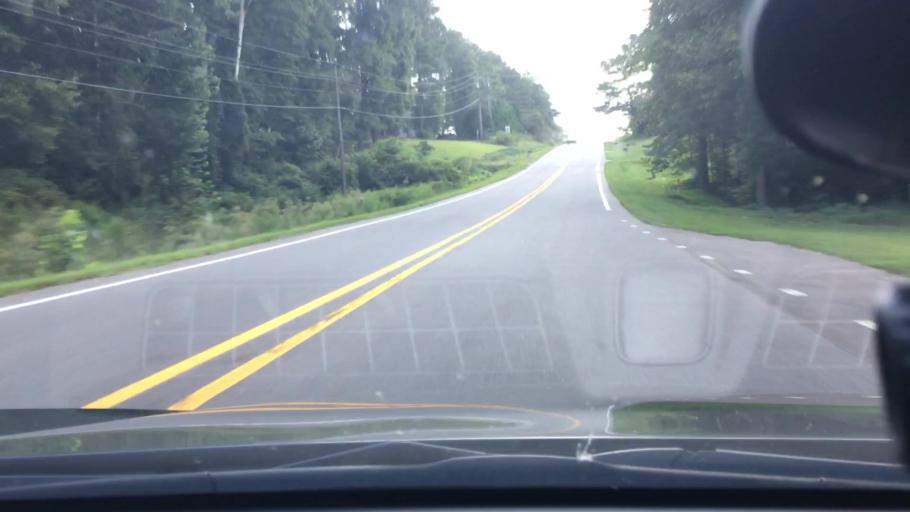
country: US
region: North Carolina
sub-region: Pitt County
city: Summerfield
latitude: 35.6426
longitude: -77.4555
